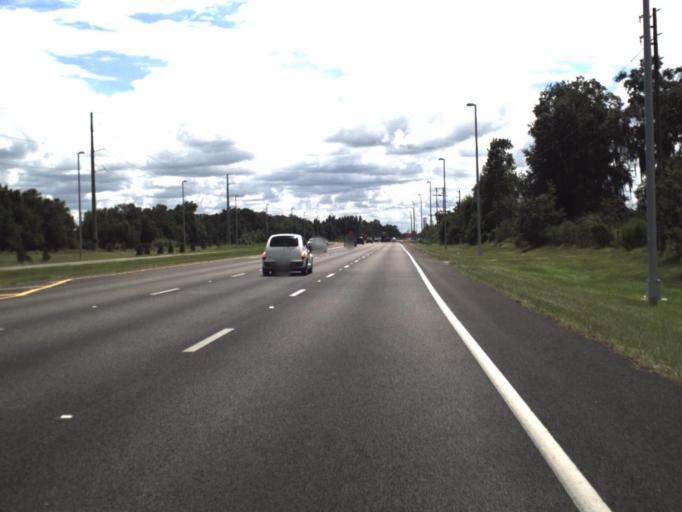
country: US
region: Florida
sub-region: Polk County
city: Highland City
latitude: 27.9345
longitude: -81.8578
